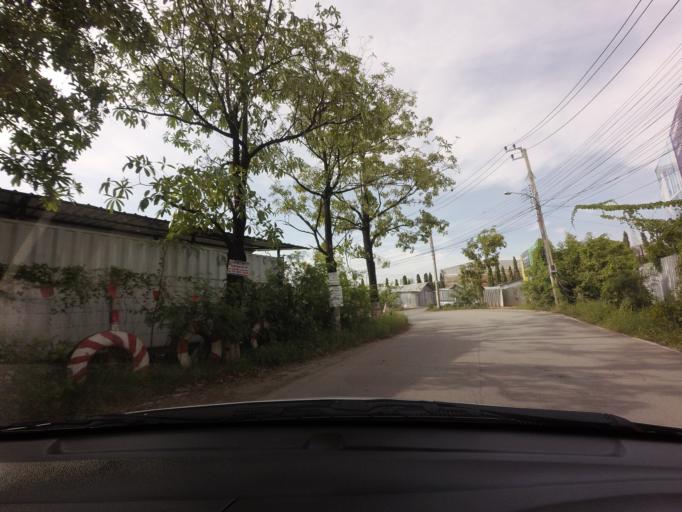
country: TH
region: Bangkok
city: Bang Na
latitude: 13.6441
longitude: 100.6613
